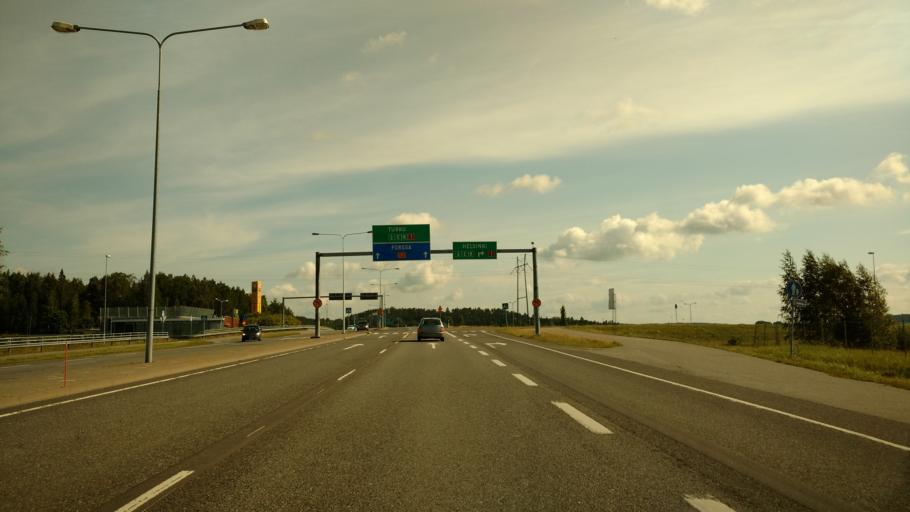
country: FI
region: Varsinais-Suomi
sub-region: Salo
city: Salo
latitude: 60.4159
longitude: 23.1639
